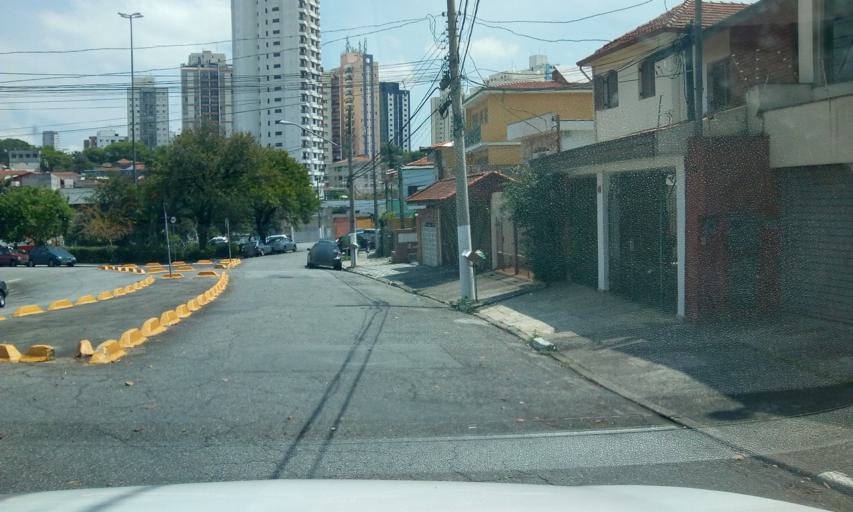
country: BR
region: Sao Paulo
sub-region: Sao Paulo
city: Sao Paulo
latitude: -23.5328
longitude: -46.7008
